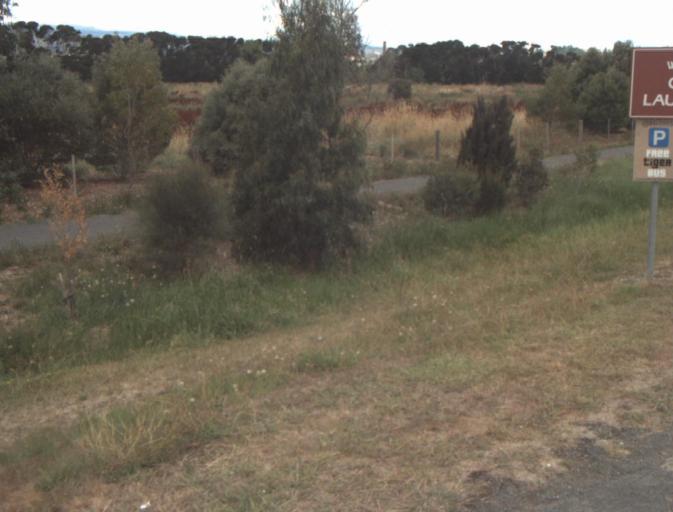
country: AU
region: Tasmania
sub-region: Launceston
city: Launceston
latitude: -41.4270
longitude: 147.1177
